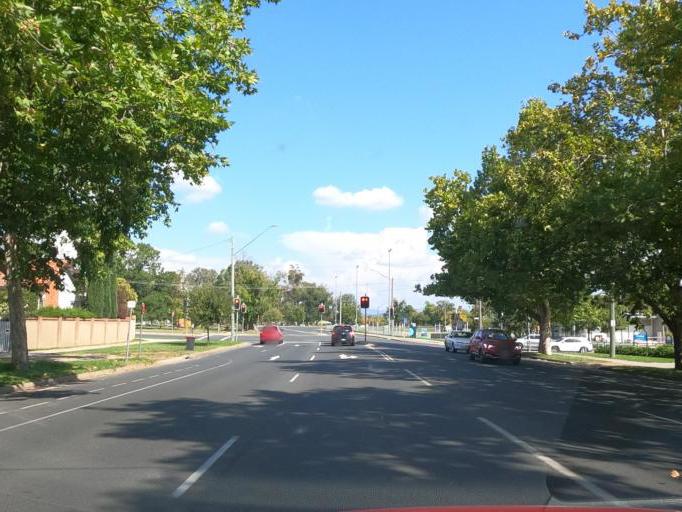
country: AU
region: New South Wales
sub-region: Albury Municipality
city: Albury
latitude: -36.0673
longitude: 146.9240
